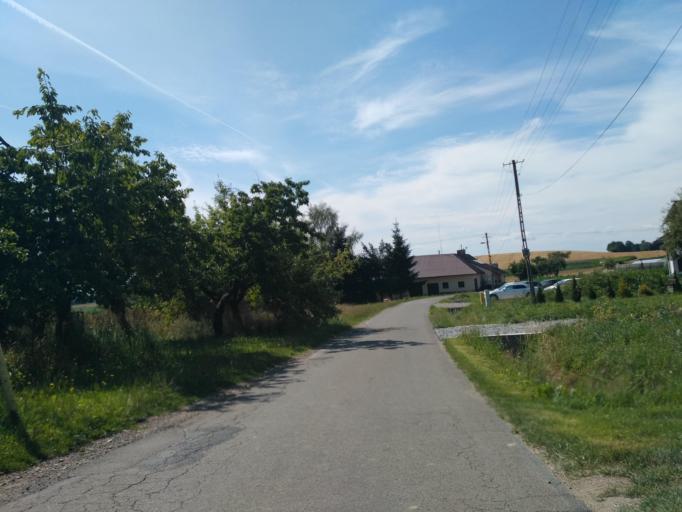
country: PL
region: Subcarpathian Voivodeship
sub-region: Powiat krosnienski
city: Kroscienko Wyzne
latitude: 49.7043
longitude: 21.8328
